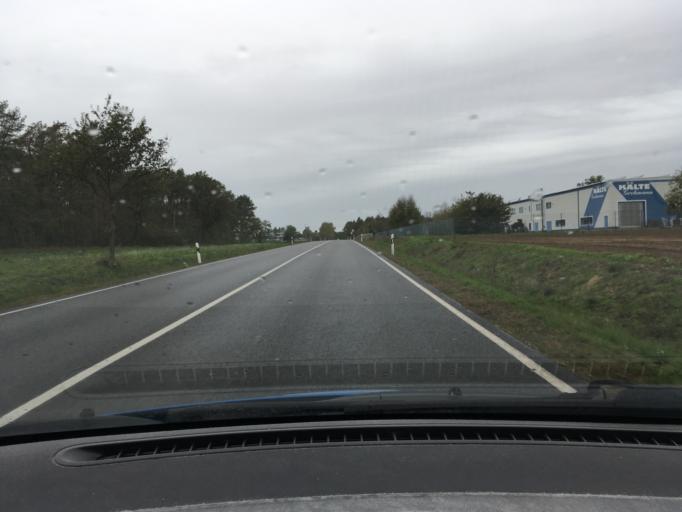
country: DE
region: Saxony-Anhalt
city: Klieken
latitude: 51.8932
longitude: 12.3751
